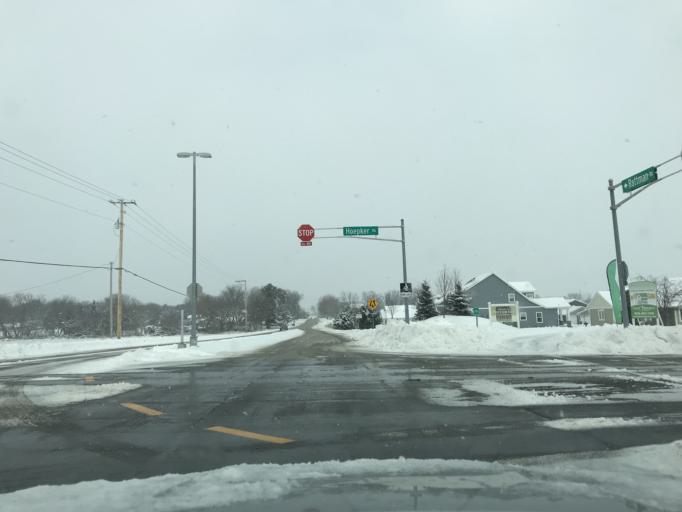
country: US
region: Wisconsin
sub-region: Dane County
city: Sun Prairie
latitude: 43.1649
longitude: -89.2850
